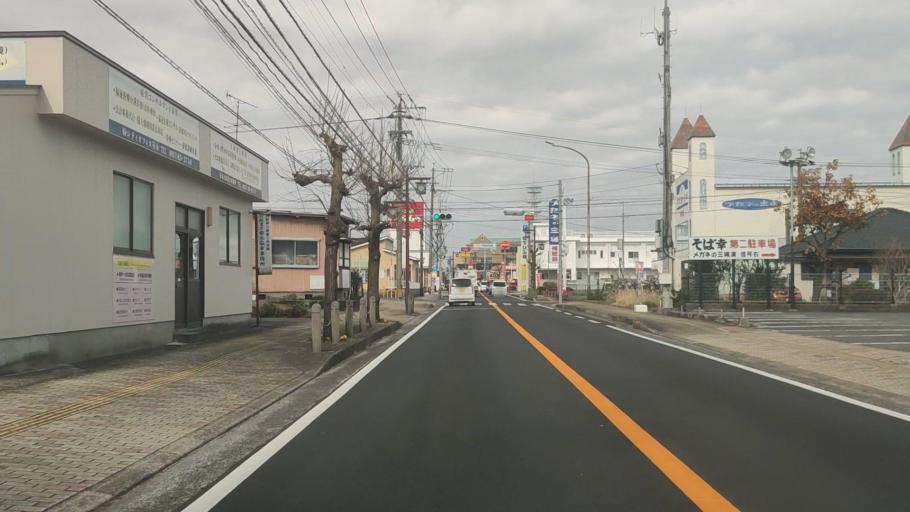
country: JP
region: Nagasaki
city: Shimabara
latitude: 32.7948
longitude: 130.3681
